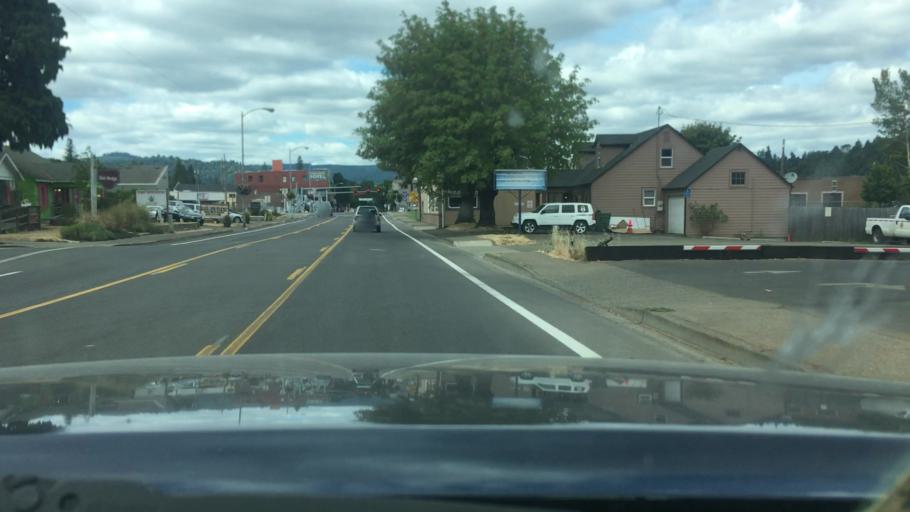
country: US
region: Oregon
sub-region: Lane County
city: Cottage Grove
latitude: 43.7973
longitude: -123.0562
